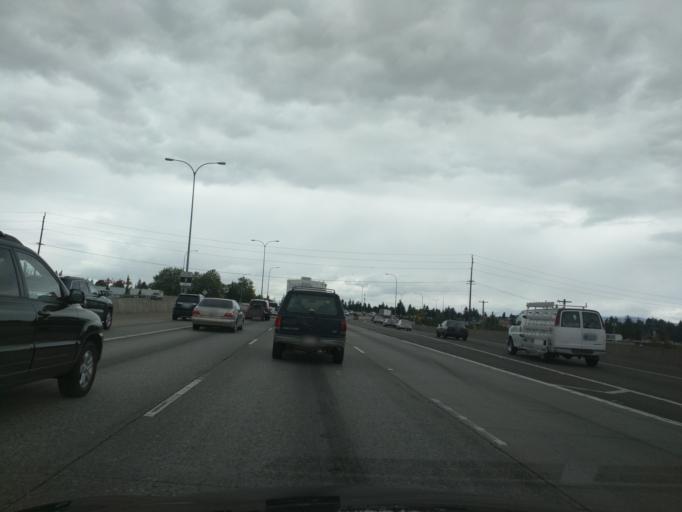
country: US
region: Washington
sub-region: Snohomish County
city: Everett
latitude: 47.9779
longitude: -122.1899
